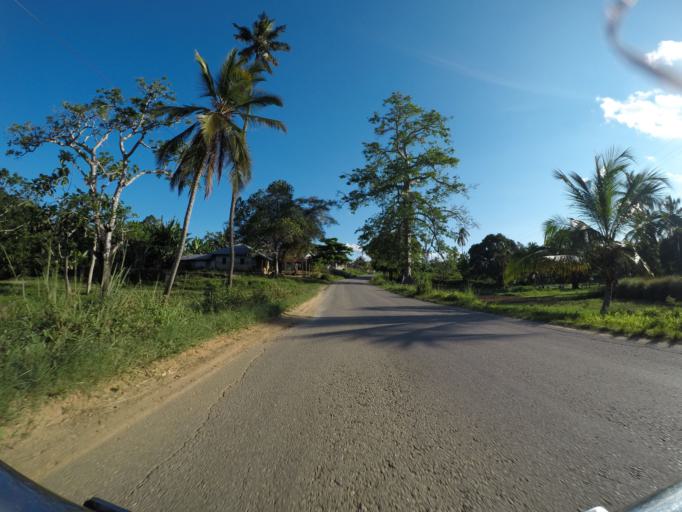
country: TZ
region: Pemba South
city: Chake Chake
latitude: -5.3097
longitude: 39.7451
